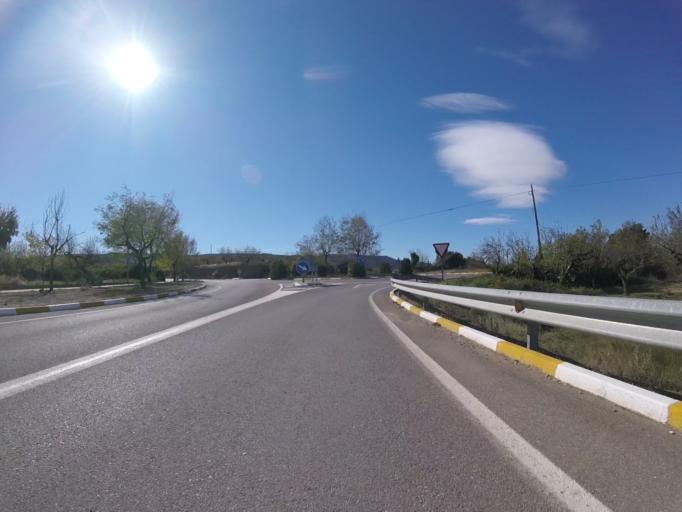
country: ES
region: Valencia
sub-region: Provincia de Castello
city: Albocasser
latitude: 40.3622
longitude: 0.0218
